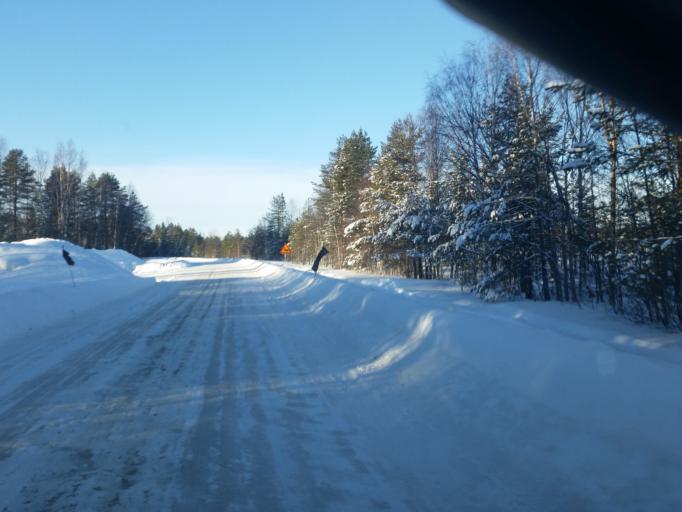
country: SE
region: Norrbotten
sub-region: Pitea Kommun
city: Roknas
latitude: 65.2024
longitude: 21.1793
